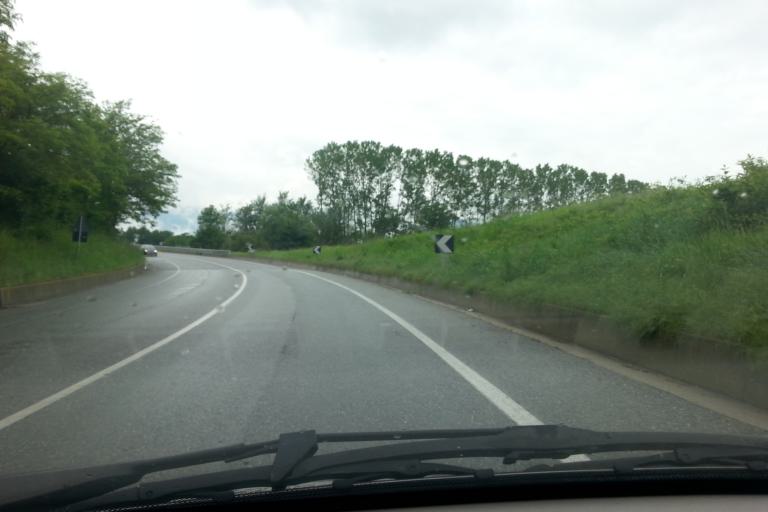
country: IT
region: Piedmont
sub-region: Provincia di Torino
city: Alpignano
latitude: 45.1168
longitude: 7.5123
